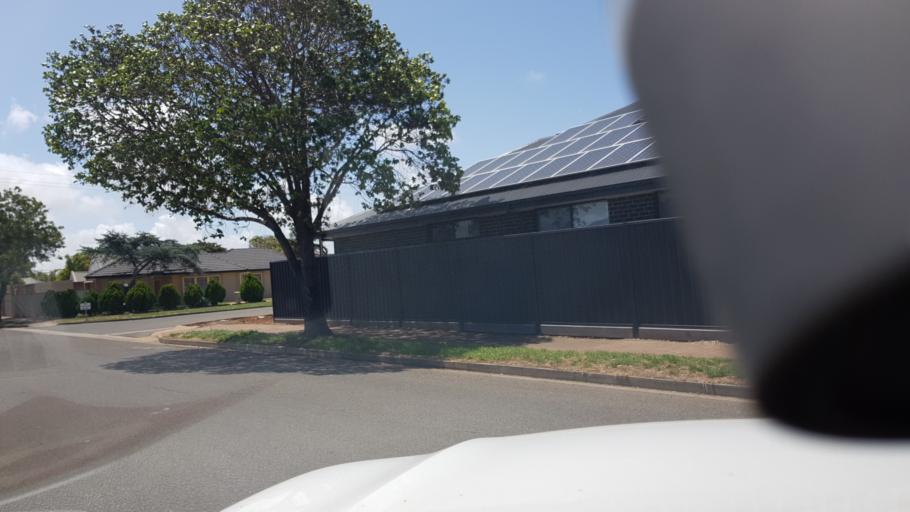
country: AU
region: South Australia
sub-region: Holdfast Bay
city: North Brighton
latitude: -35.0007
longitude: 138.5295
